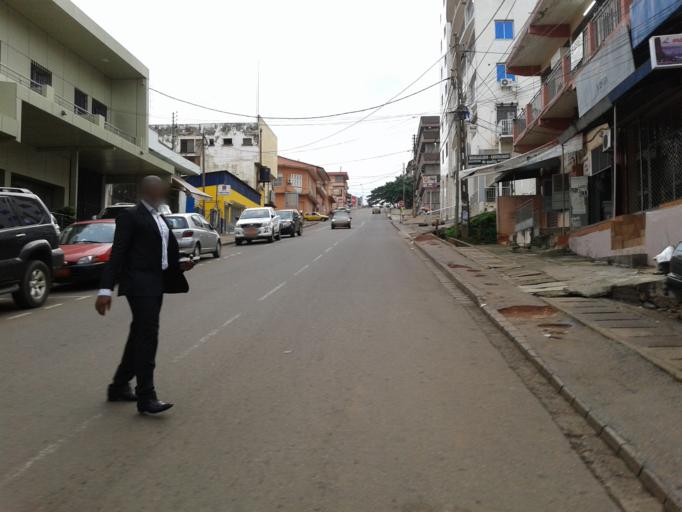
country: CM
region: Centre
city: Yaounde
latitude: 3.8702
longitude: 11.5157
